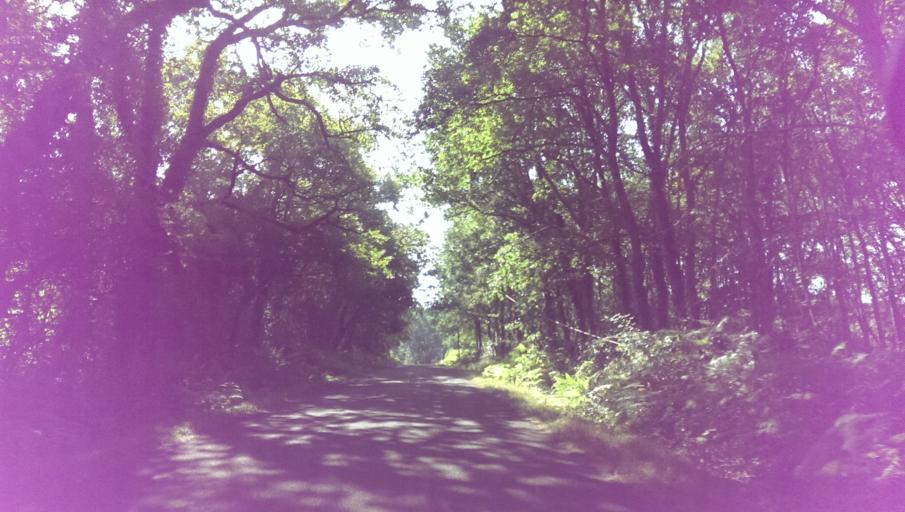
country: FR
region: Aquitaine
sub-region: Departement des Landes
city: Sarbazan
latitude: 44.0383
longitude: -0.1723
